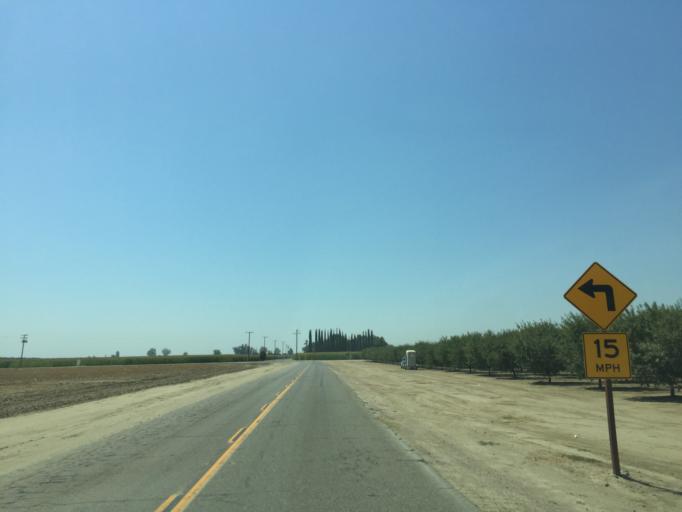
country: US
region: California
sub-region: Tulare County
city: Goshen
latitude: 36.3709
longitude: -119.4189
